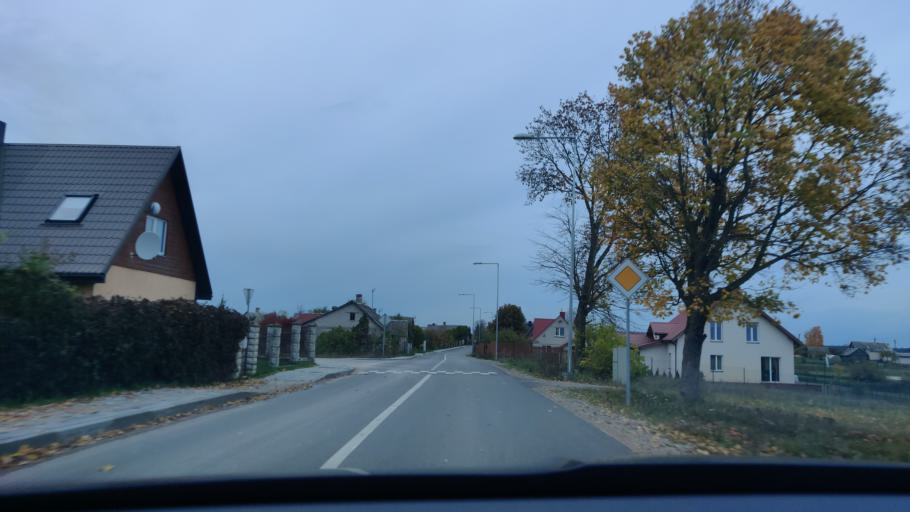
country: LT
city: Lentvaris
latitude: 54.5813
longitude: 25.0515
